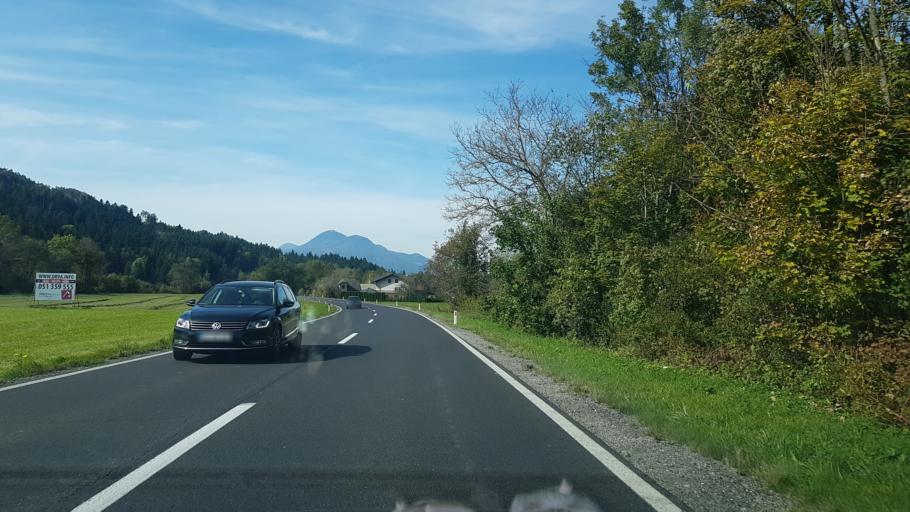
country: SI
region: Slovenj Gradec
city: Legen
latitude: 46.4486
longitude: 15.1685
